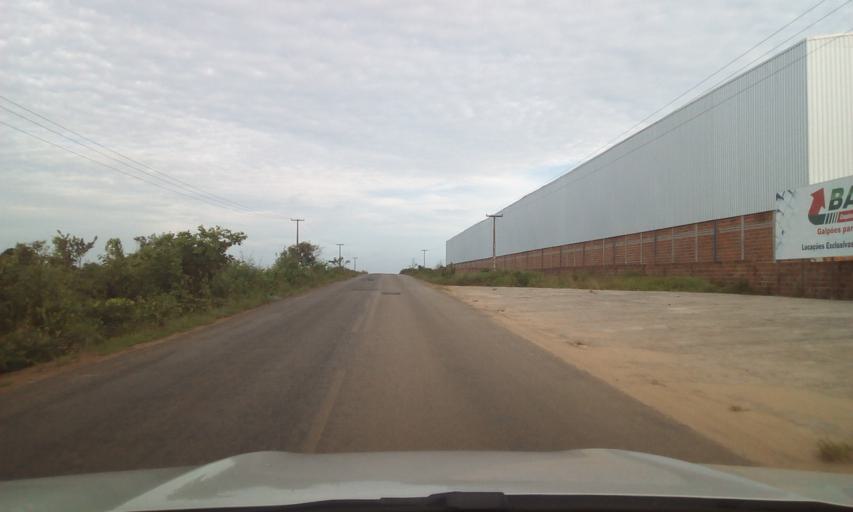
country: BR
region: Paraiba
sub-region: Conde
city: Conde
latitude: -7.2717
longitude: -34.8738
